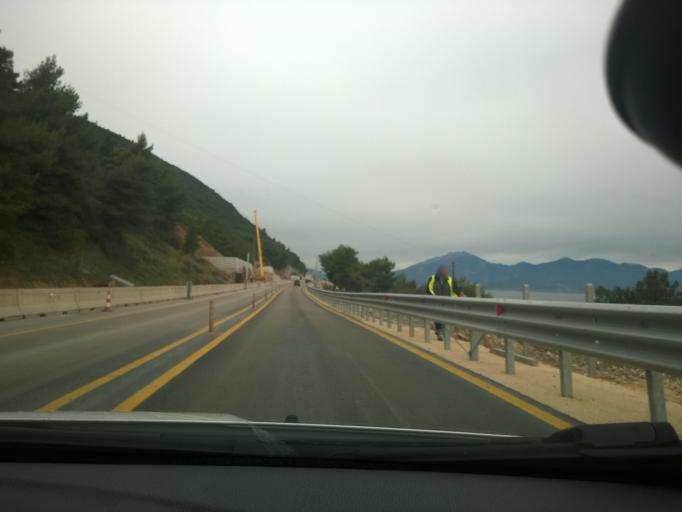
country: GR
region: West Greece
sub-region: Nomos Achaias
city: Kamarai
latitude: 38.3205
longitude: 21.9709
